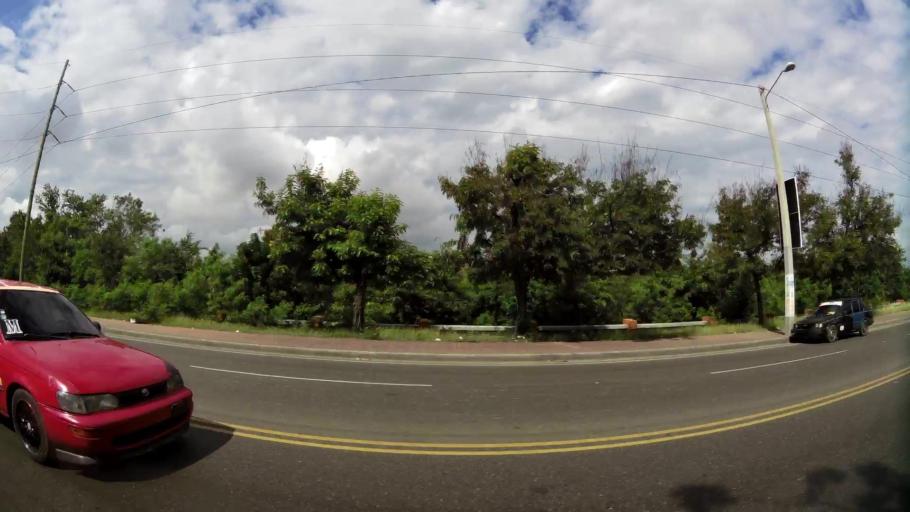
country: DO
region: Santiago
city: Santiago de los Caballeros
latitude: 19.4640
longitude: -70.7128
